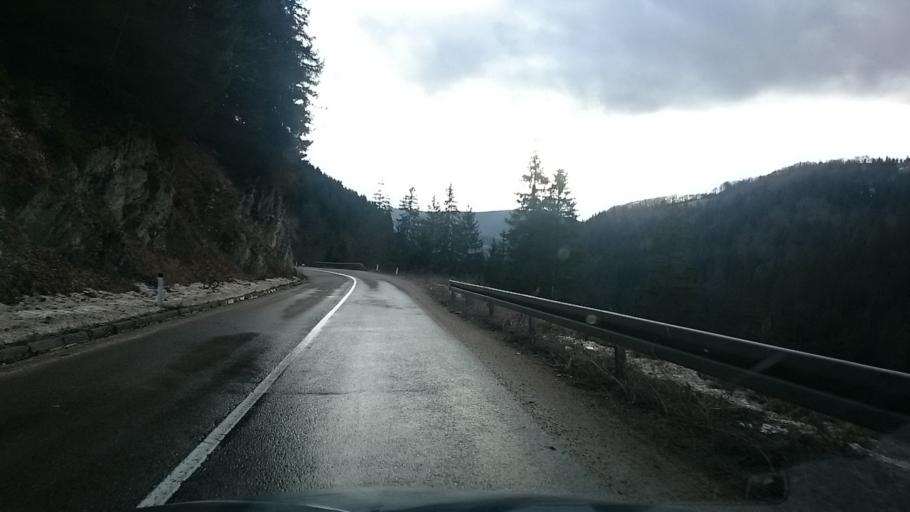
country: BA
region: Republika Srpska
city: Skender Vakuf
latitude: 44.4714
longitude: 17.3792
